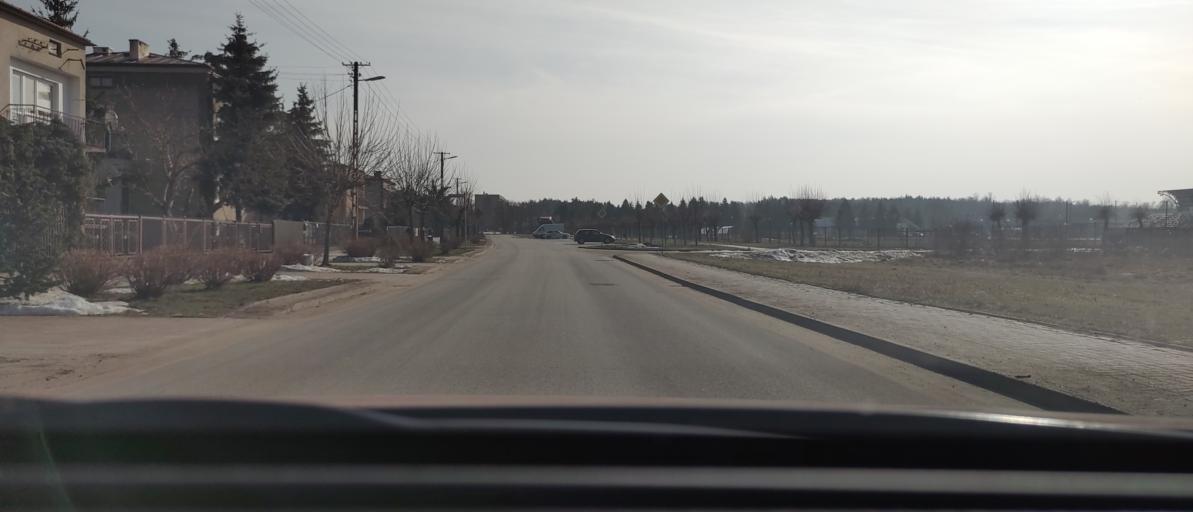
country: PL
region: Masovian Voivodeship
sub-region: Powiat bialobrzeski
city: Bialobrzegi
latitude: 51.6469
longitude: 20.9442
